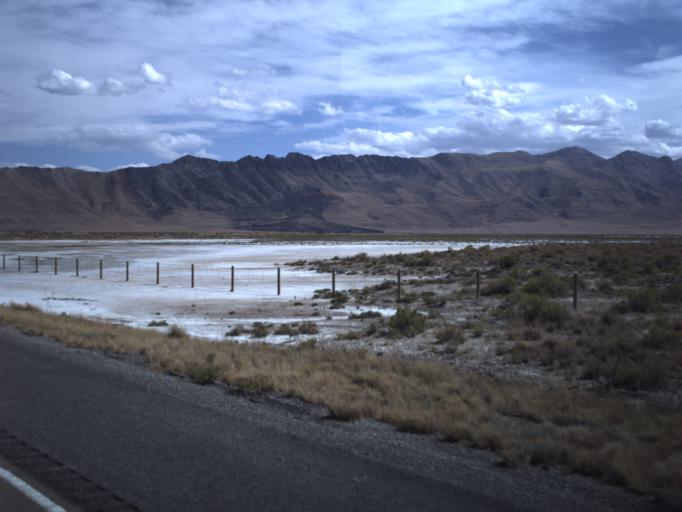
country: US
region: Utah
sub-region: Tooele County
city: Grantsville
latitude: 40.7499
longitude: -112.6957
